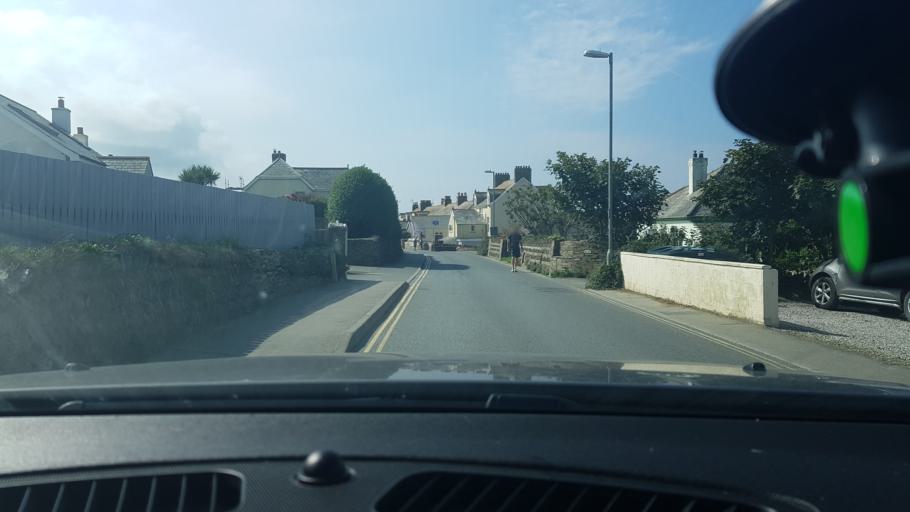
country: GB
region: England
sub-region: Cornwall
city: Tintagel
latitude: 50.6657
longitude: -4.7526
